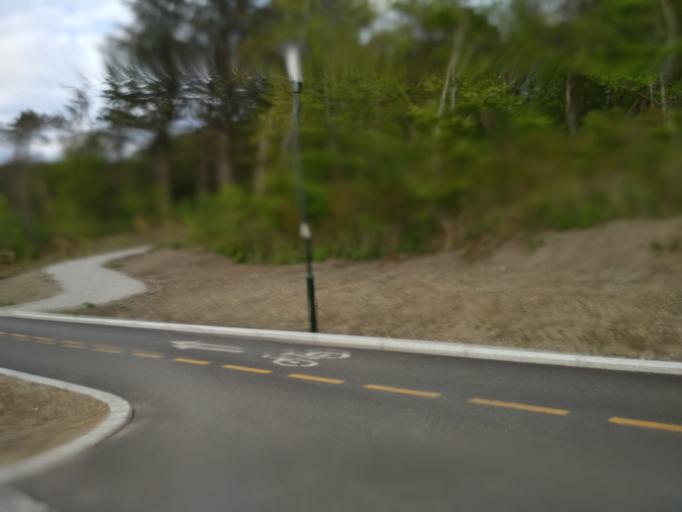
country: NO
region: Rogaland
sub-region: Stavanger
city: Stavanger
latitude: 58.9558
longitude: 5.7229
